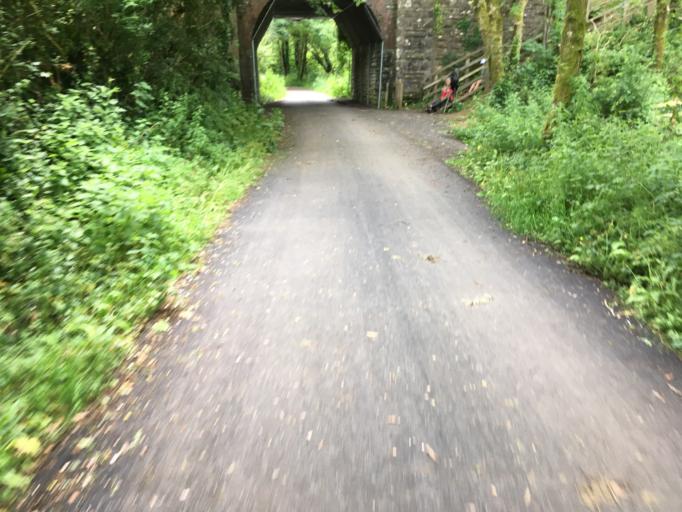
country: GB
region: England
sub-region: Cornwall
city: Wadebridge
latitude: 50.4920
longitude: -4.8014
